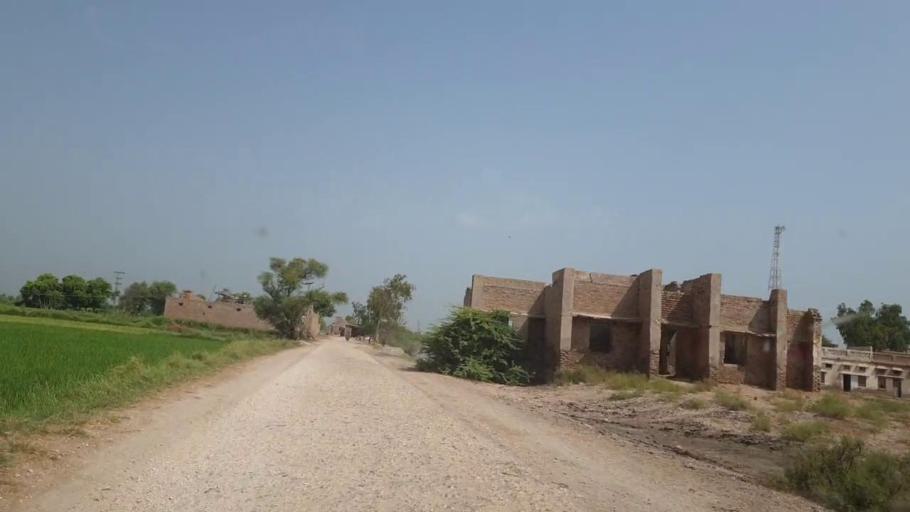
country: PK
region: Sindh
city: Lakhi
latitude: 27.8704
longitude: 68.6605
